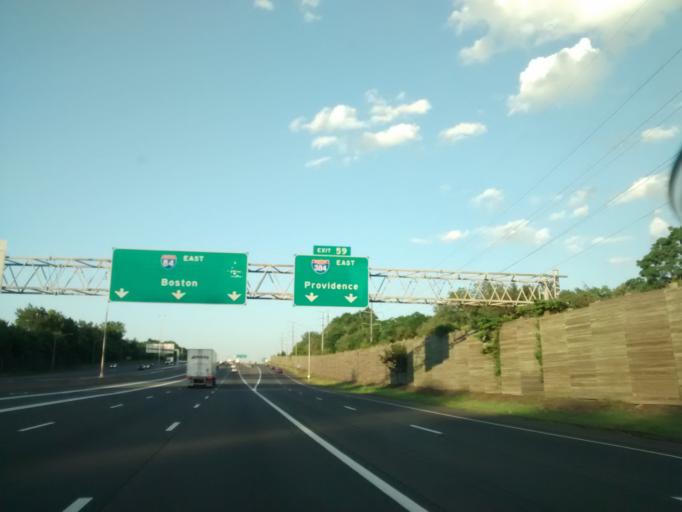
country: US
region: Connecticut
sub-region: Hartford County
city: East Hartford
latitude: 41.7717
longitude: -72.5982
